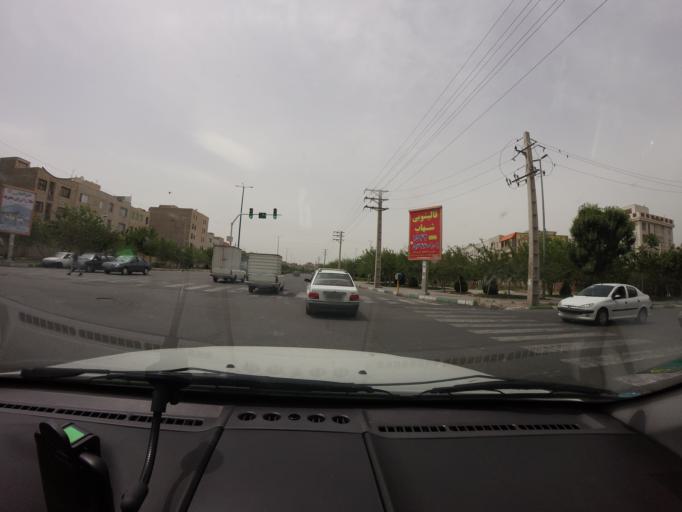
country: IR
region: Tehran
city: Eslamshahr
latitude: 35.5339
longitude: 51.2171
